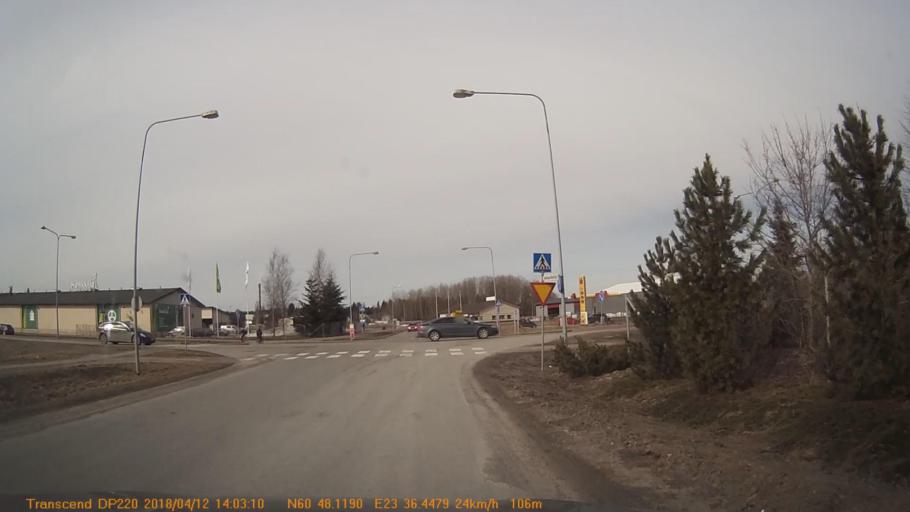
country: FI
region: Haeme
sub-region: Forssa
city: Forssa
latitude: 60.8021
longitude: 23.6073
